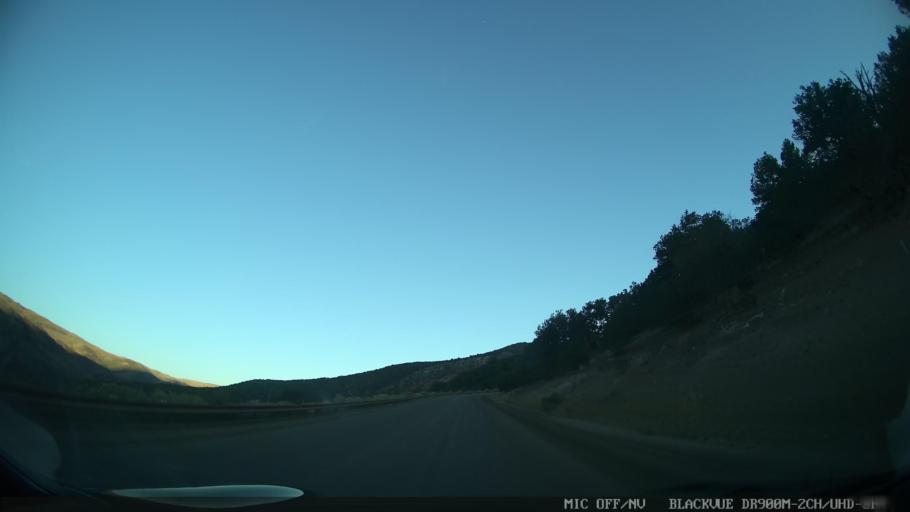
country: US
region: Colorado
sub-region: Eagle County
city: Edwards
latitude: 39.8589
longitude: -106.6433
